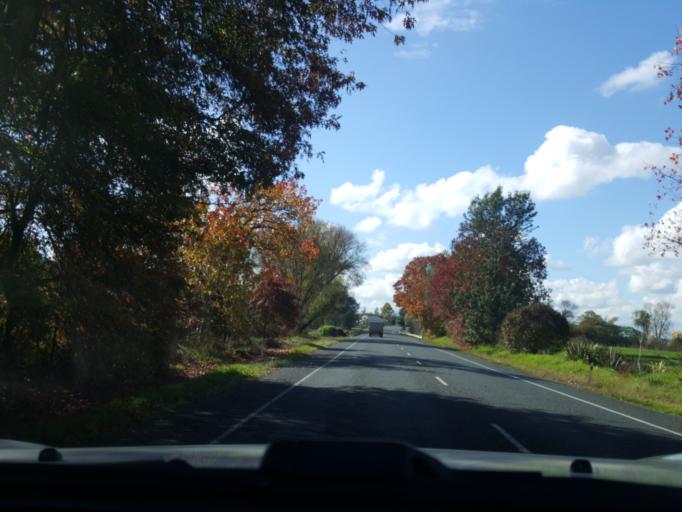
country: NZ
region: Waikato
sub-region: Waikato District
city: Ngaruawahia
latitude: -37.6295
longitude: 175.1786
